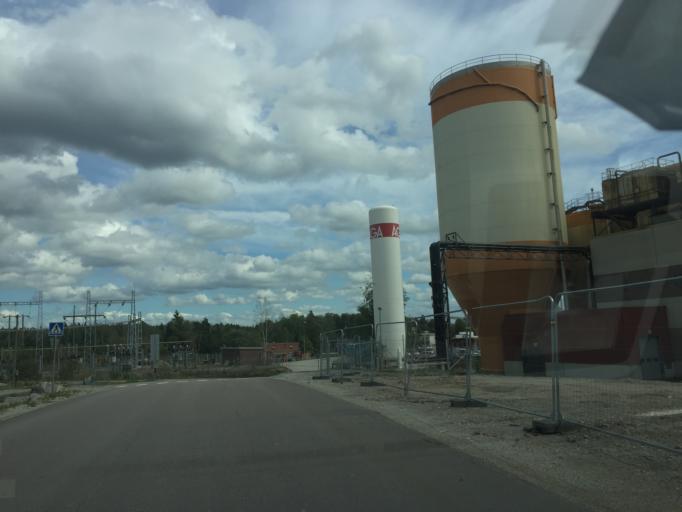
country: SE
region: OErebro
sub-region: Lindesbergs Kommun
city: Frovi
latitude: 59.4822
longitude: 15.3211
